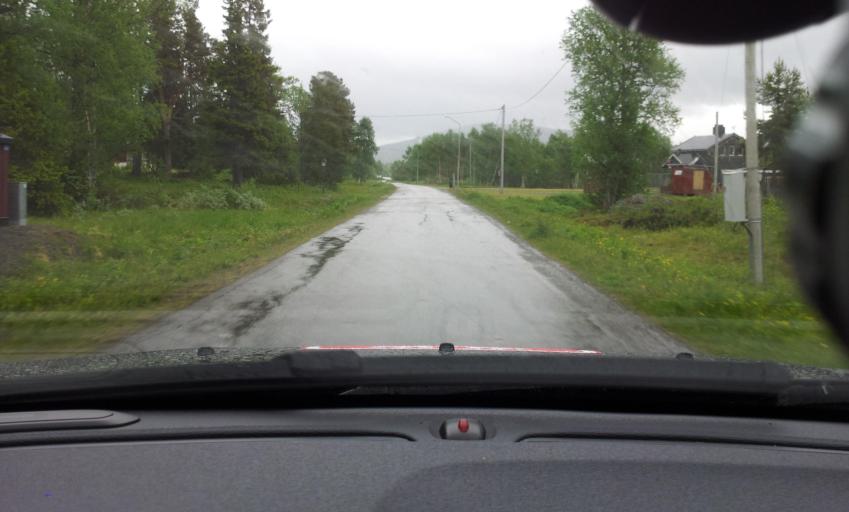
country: SE
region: Jaemtland
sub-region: Are Kommun
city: Are
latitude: 63.1480
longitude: 12.9558
